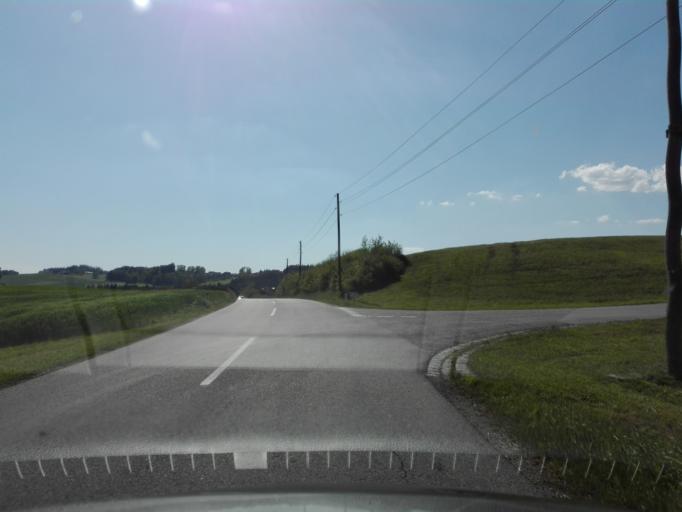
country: DE
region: Bavaria
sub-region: Lower Bavaria
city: Obernzell
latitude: 48.4581
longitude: 13.6157
